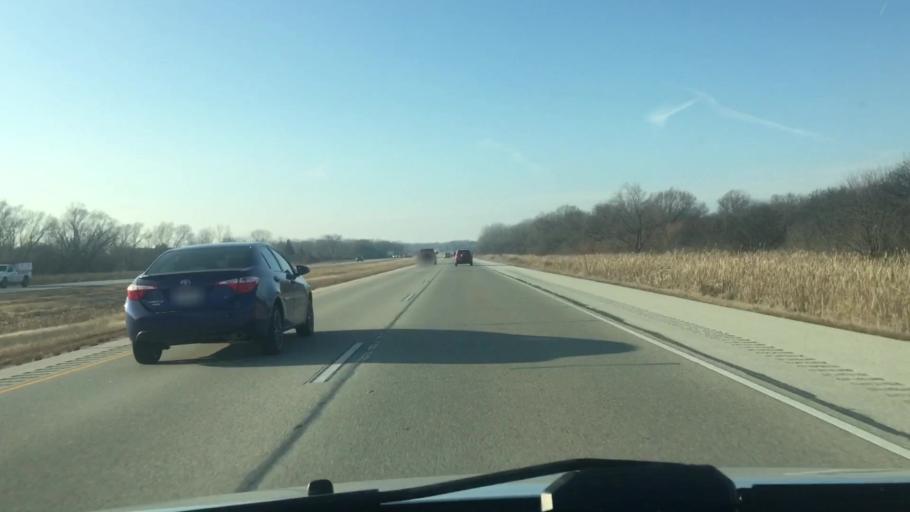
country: US
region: Wisconsin
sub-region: Waukesha County
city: Pewaukee
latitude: 43.0992
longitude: -88.2911
